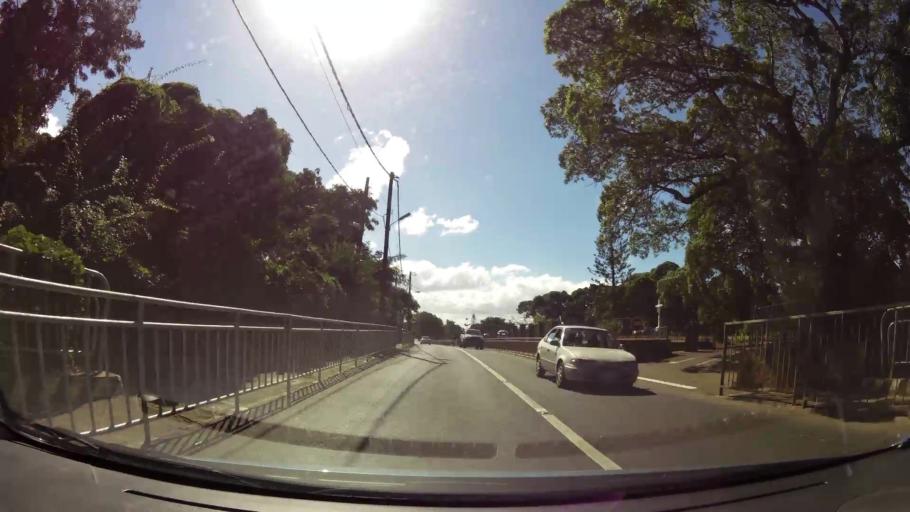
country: MU
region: Black River
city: Cascavelle
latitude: -20.2556
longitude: 57.4189
